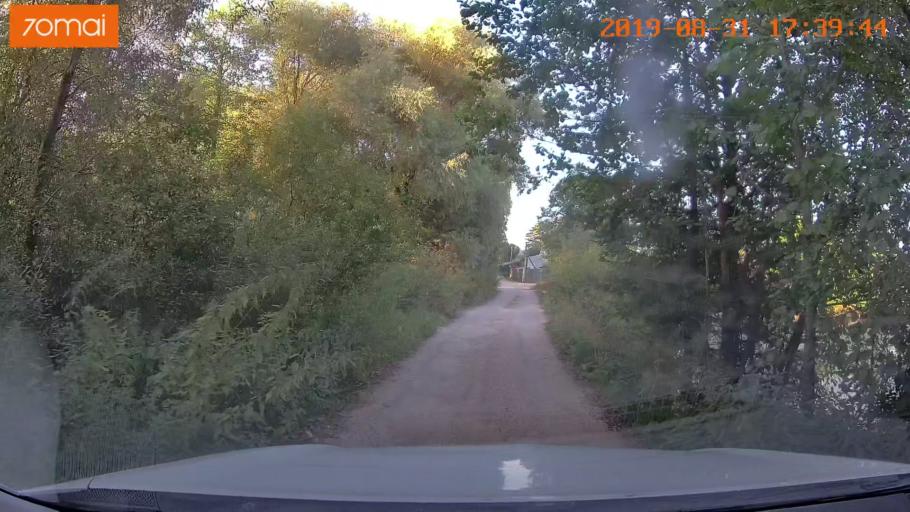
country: RU
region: Kaluga
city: Detchino
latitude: 54.8181
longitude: 36.3639
